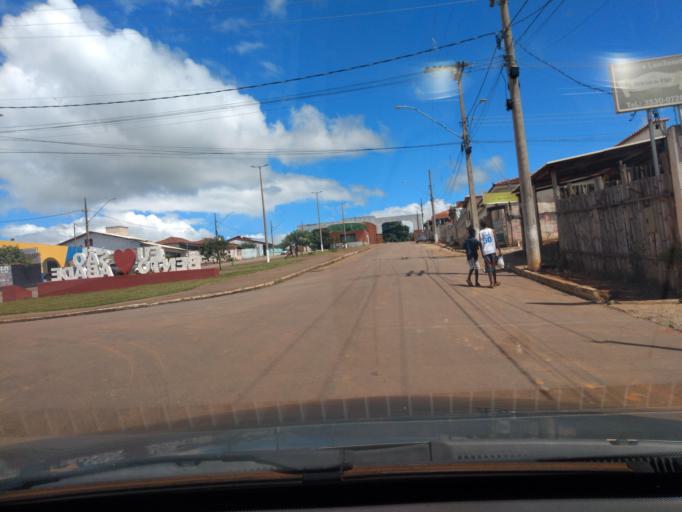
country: BR
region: Minas Gerais
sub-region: Tres Coracoes
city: Tres Coracoes
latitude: -21.5893
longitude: -45.0679
